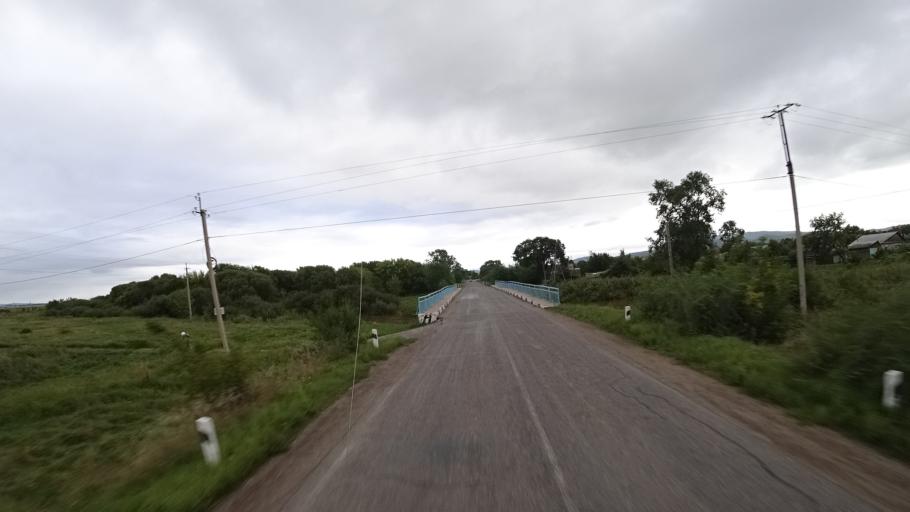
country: RU
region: Primorskiy
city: Chernigovka
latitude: 44.3532
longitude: 132.5667
